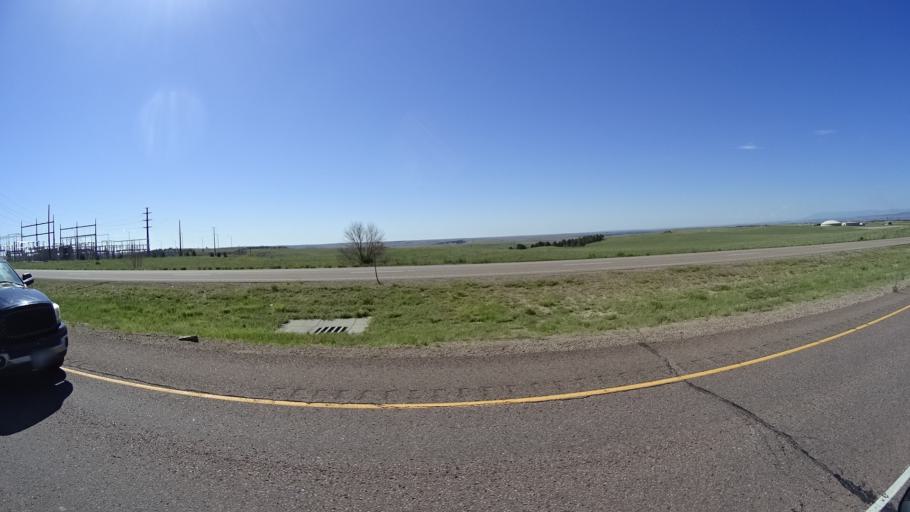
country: US
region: Colorado
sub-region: El Paso County
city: Cimarron Hills
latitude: 38.8580
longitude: -104.6739
